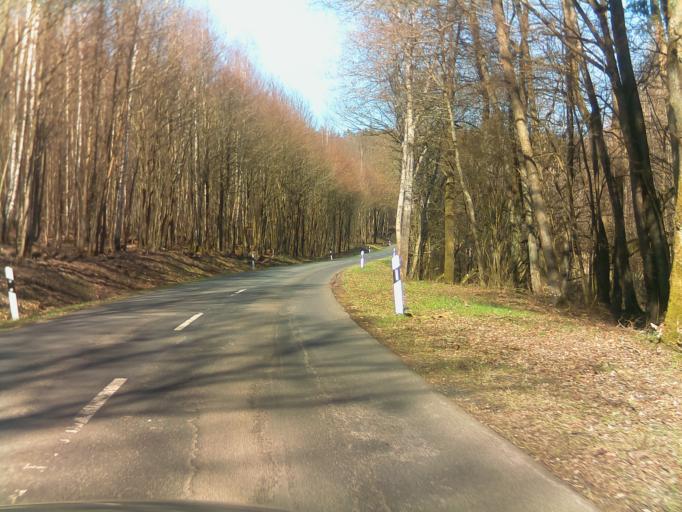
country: DE
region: Bavaria
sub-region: Regierungsbezirk Unterfranken
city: Willmars
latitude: 50.4870
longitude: 10.2650
